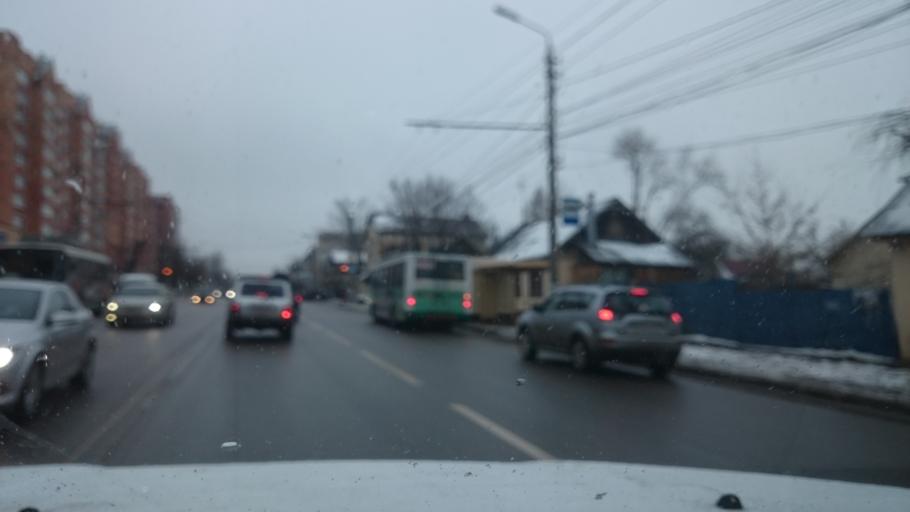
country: RU
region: Tula
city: Mendeleyevskiy
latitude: 54.1774
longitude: 37.5741
